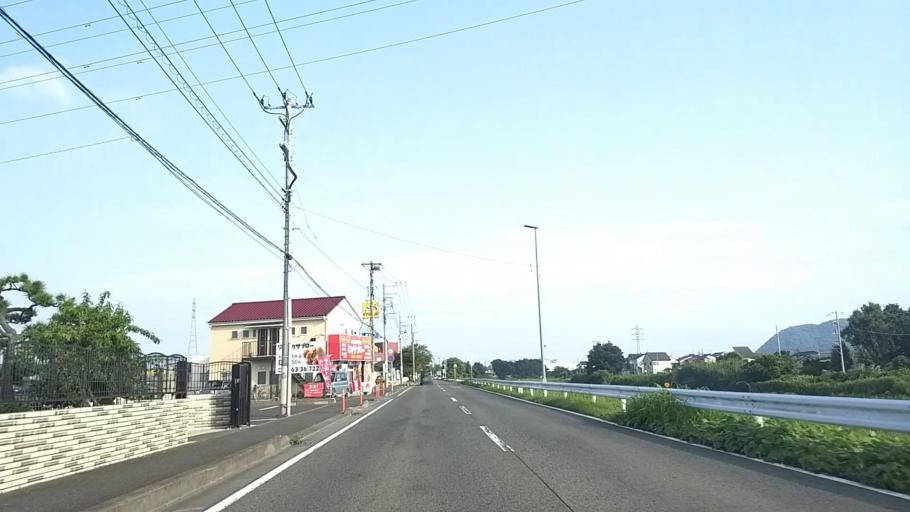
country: JP
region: Kanagawa
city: Hiratsuka
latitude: 35.3464
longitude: 139.3180
